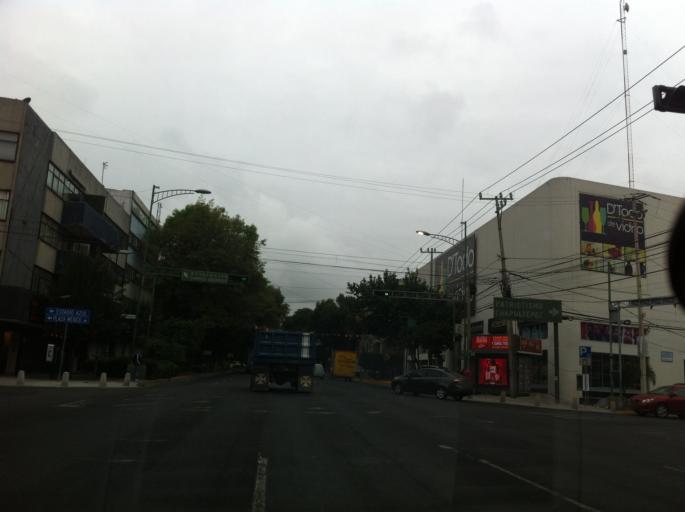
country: MX
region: Mexico City
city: Colonia del Valle
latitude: 19.3859
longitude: -99.1764
